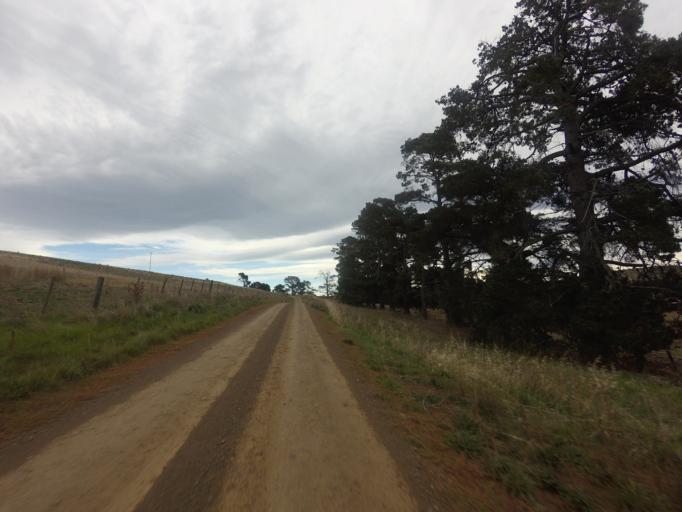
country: AU
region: Tasmania
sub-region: Derwent Valley
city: New Norfolk
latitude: -42.4490
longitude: 146.7856
